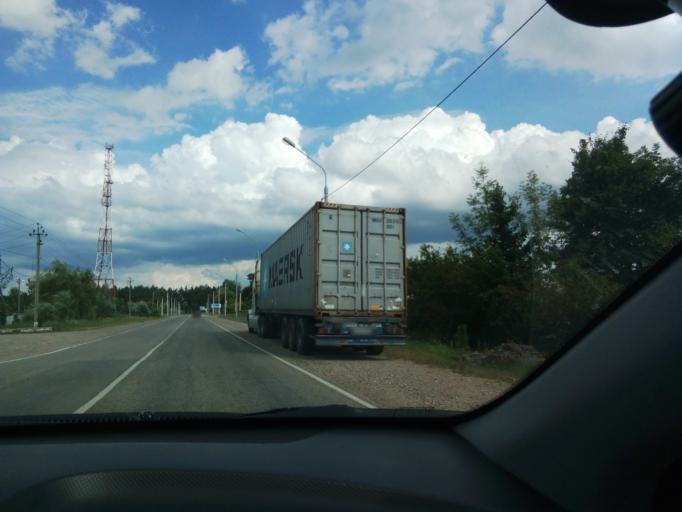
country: RU
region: Krasnodarskiy
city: Apsheronsk
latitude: 44.4380
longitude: 39.7591
